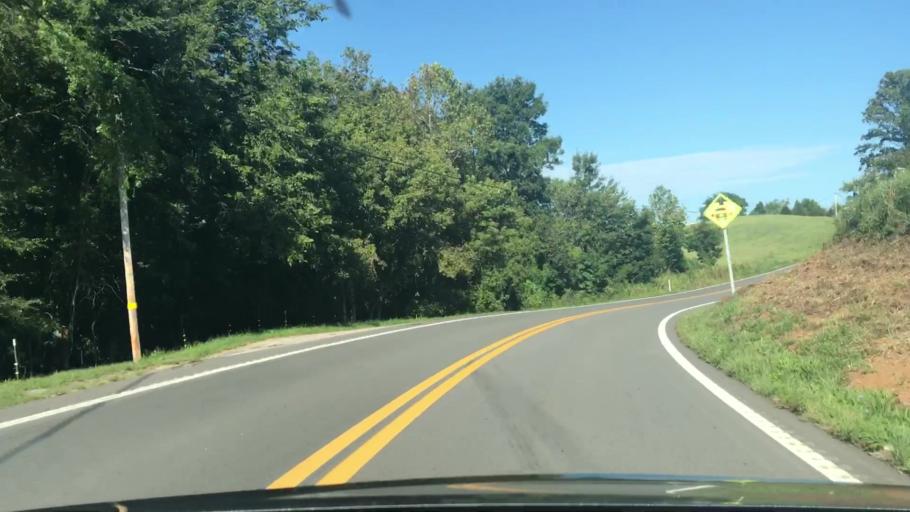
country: US
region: Tennessee
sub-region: Pickett County
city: Byrdstown
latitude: 36.6172
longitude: -85.0778
